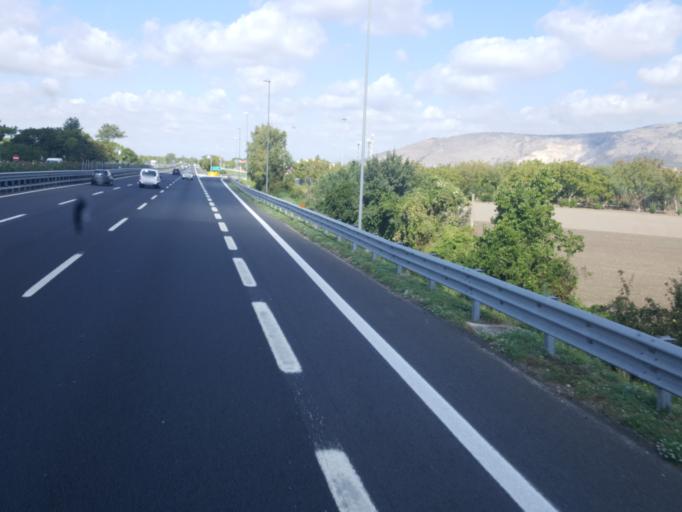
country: IT
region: Campania
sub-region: Provincia di Napoli
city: San Vitaliano
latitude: 40.9506
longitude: 14.4743
